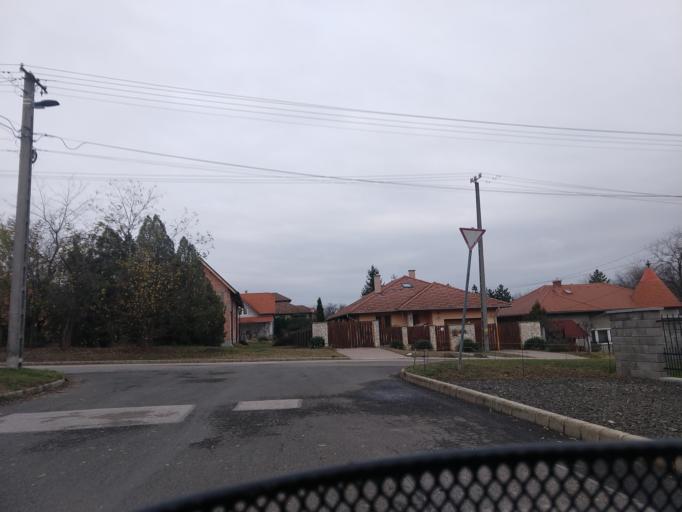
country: HU
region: Pest
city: Orbottyan
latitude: 47.6748
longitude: 19.2843
